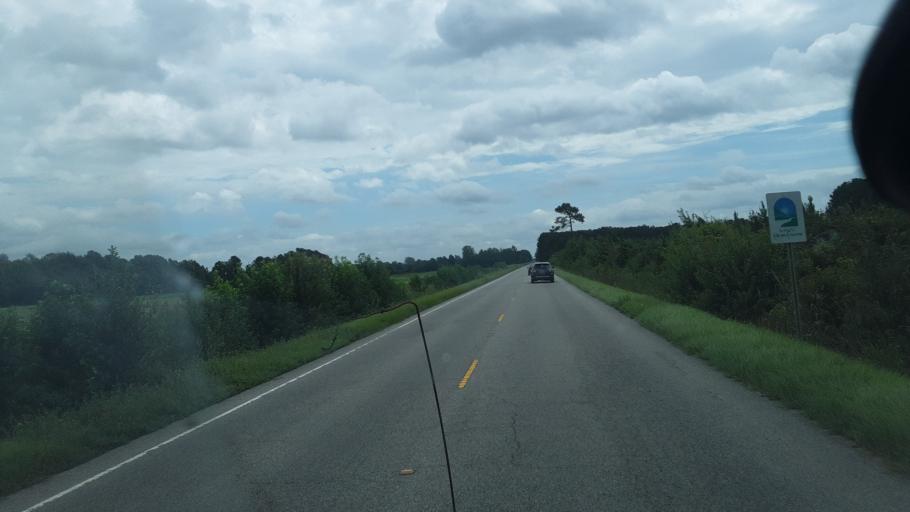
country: US
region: North Carolina
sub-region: Robeson County
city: Maxton
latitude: 34.6750
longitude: -79.4149
